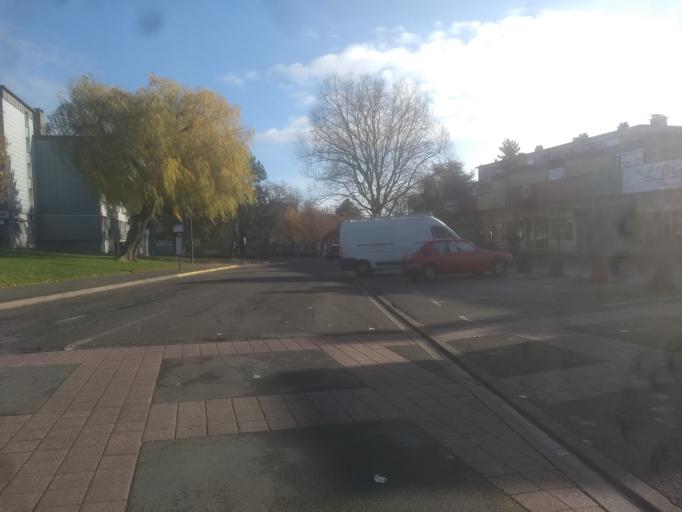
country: FR
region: Nord-Pas-de-Calais
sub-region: Departement du Pas-de-Calais
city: Anzin-Saint-Aubin
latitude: 50.3008
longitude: 2.7466
